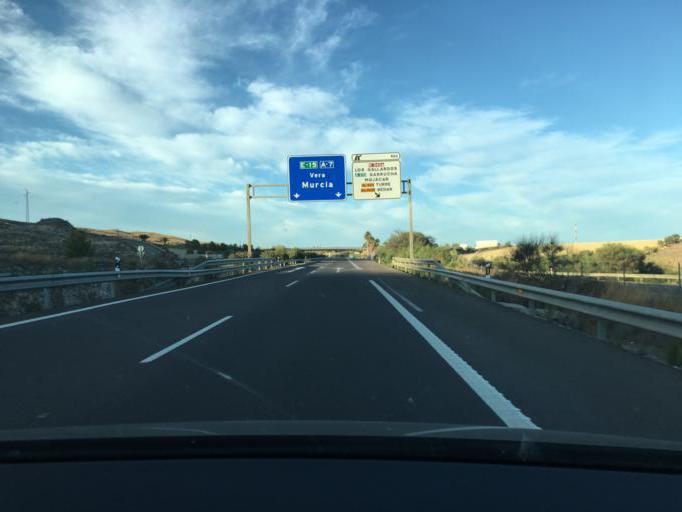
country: ES
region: Andalusia
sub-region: Provincia de Almeria
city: Bedar
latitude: 37.1542
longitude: -1.9535
